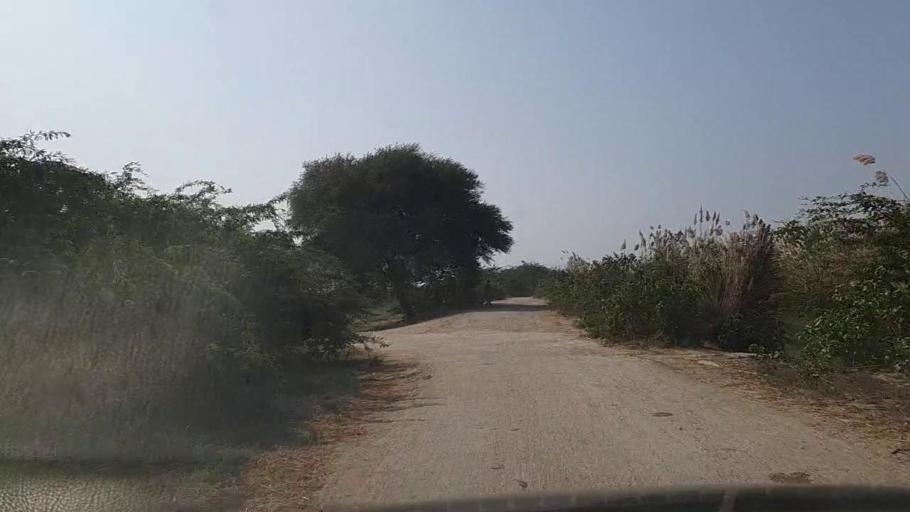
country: PK
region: Sindh
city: Gharo
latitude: 24.7051
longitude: 67.6471
